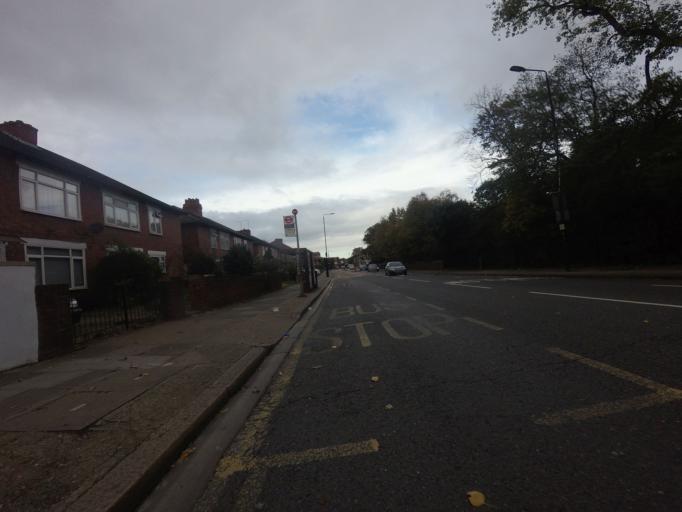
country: GB
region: England
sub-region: Greater London
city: East Ham
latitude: 51.5215
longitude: 0.0582
